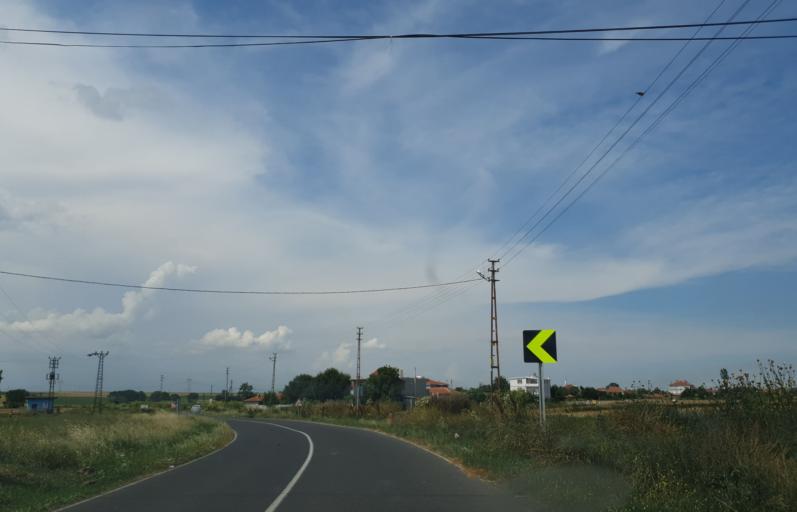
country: TR
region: Tekirdag
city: Muratli
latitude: 41.2147
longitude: 27.5408
